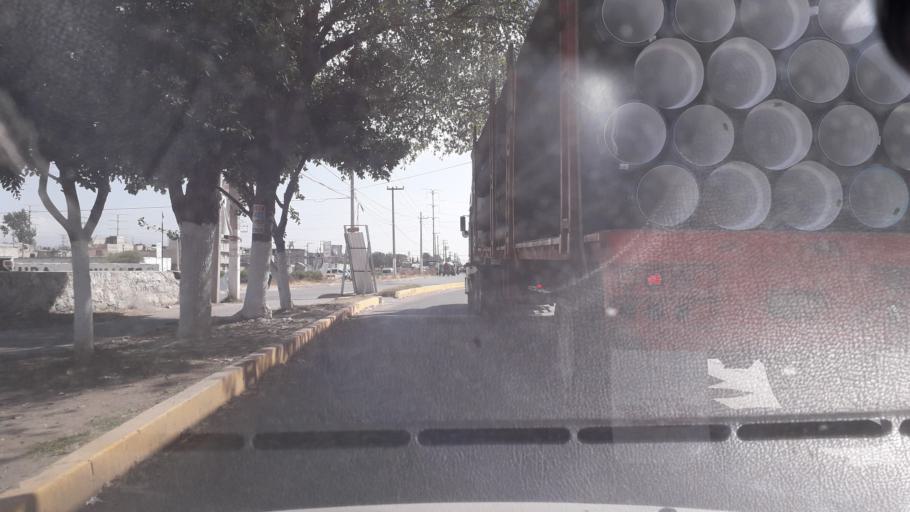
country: MX
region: Mexico
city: Ecatepec
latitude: 19.6401
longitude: -99.0580
